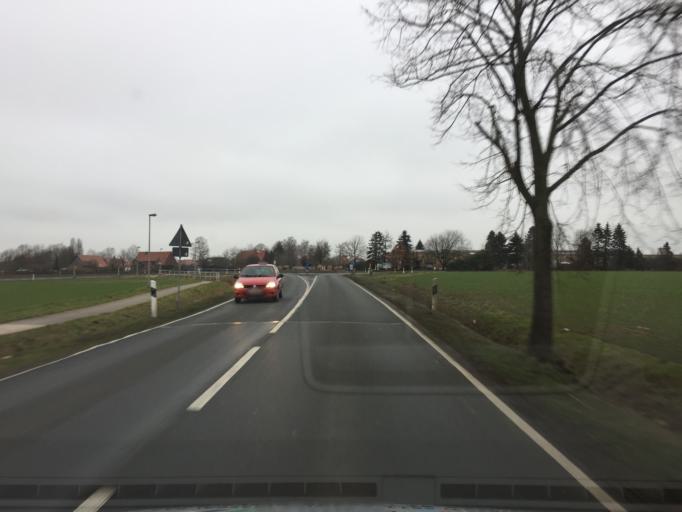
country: DE
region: Lower Saxony
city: Wiedensahl
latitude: 52.3730
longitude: 9.1268
